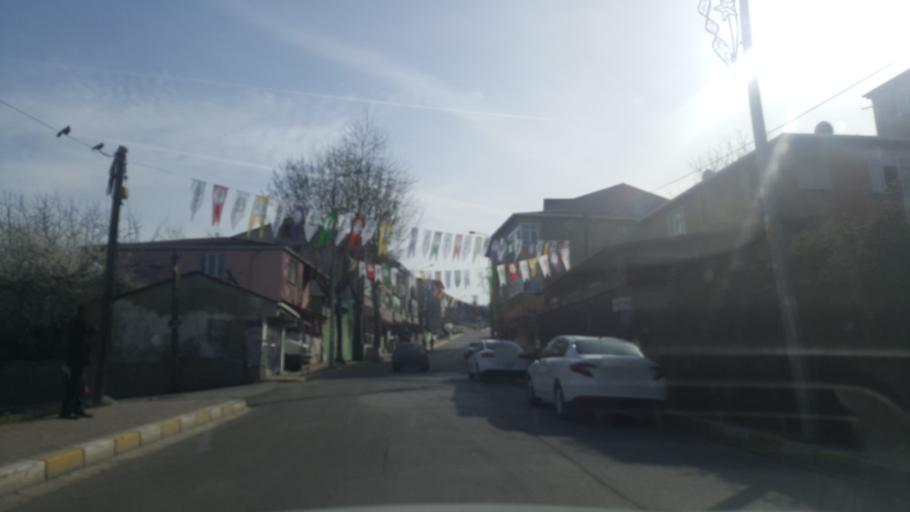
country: TR
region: Kocaeli
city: Tavsancil
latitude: 40.7858
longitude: 29.5543
